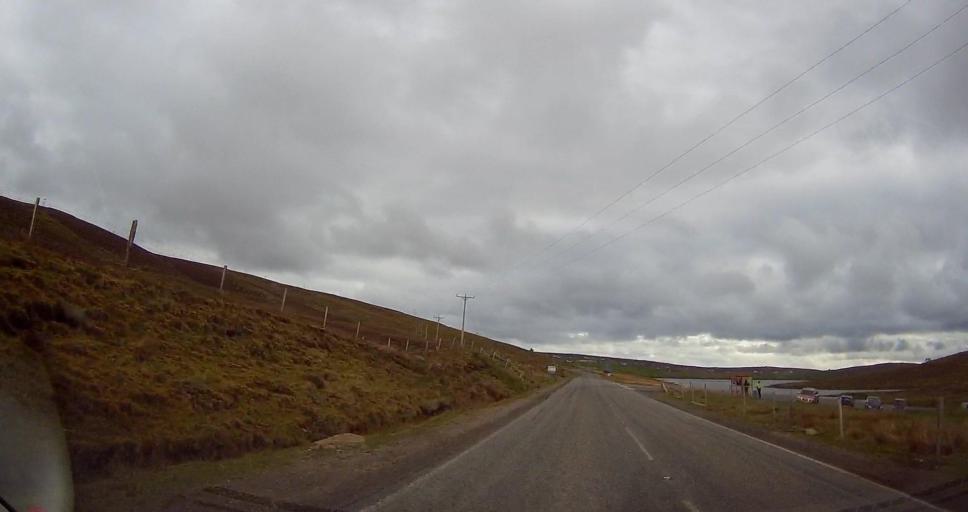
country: GB
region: Scotland
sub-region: Shetland Islands
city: Shetland
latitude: 60.6050
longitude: -1.0932
